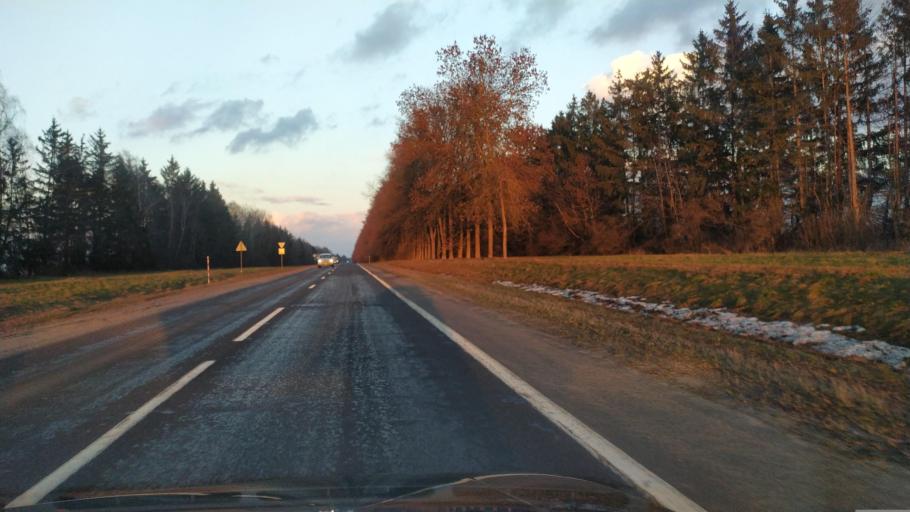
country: BY
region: Brest
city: Kamyanyets
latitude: 52.3714
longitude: 23.7947
